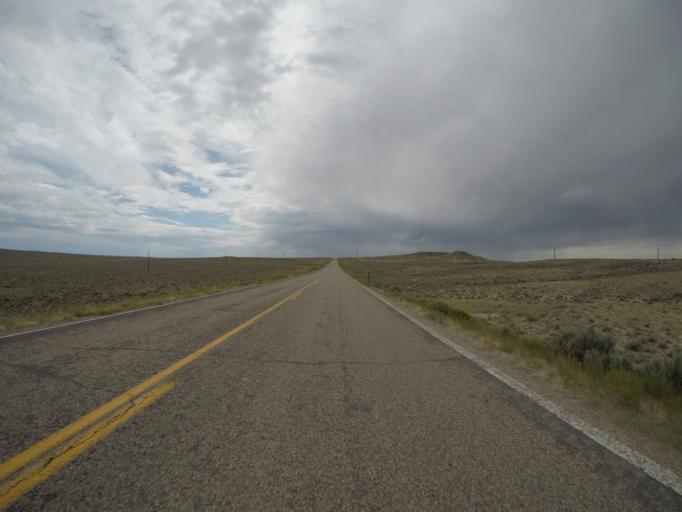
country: US
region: Wyoming
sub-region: Lincoln County
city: Kemmerer
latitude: 41.9761
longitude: -110.0740
